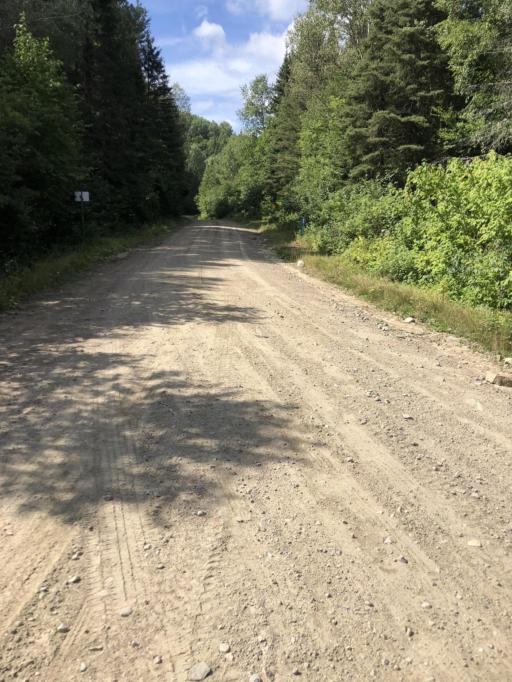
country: CA
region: Quebec
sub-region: Saguenay/Lac-Saint-Jean
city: Saguenay
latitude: 48.0492
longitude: -70.6159
